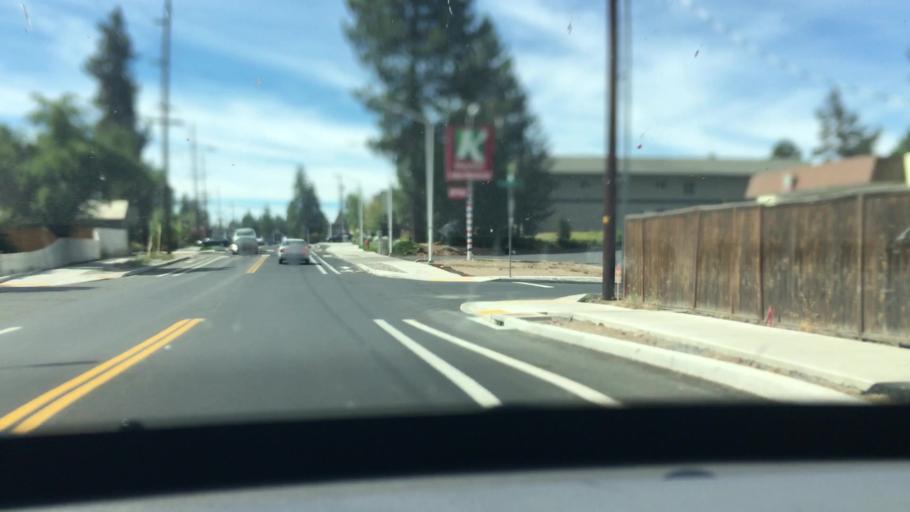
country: US
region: Oregon
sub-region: Deschutes County
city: Bend
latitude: 44.0521
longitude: -121.3318
